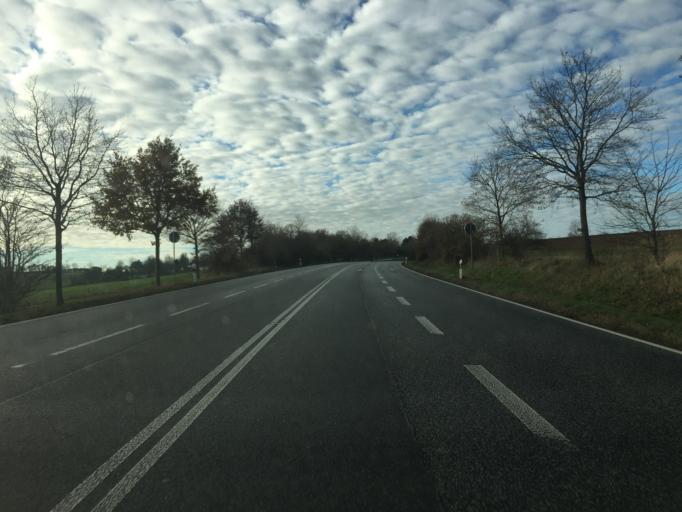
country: DE
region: North Rhine-Westphalia
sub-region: Regierungsbezirk Koln
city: Kall
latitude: 50.5594
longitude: 6.5744
